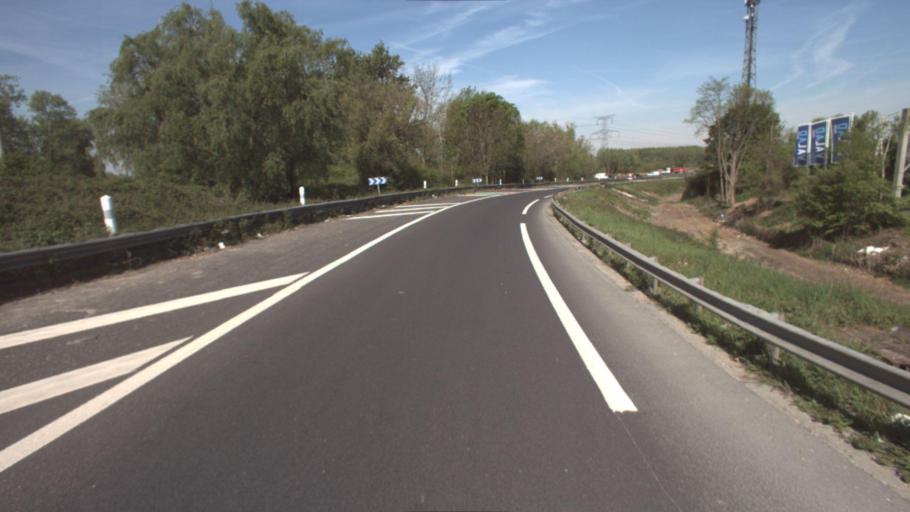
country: FR
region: Ile-de-France
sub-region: Departement de Seine-et-Marne
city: Saint-Thibault-des-Vignes
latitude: 48.8673
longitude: 2.6729
